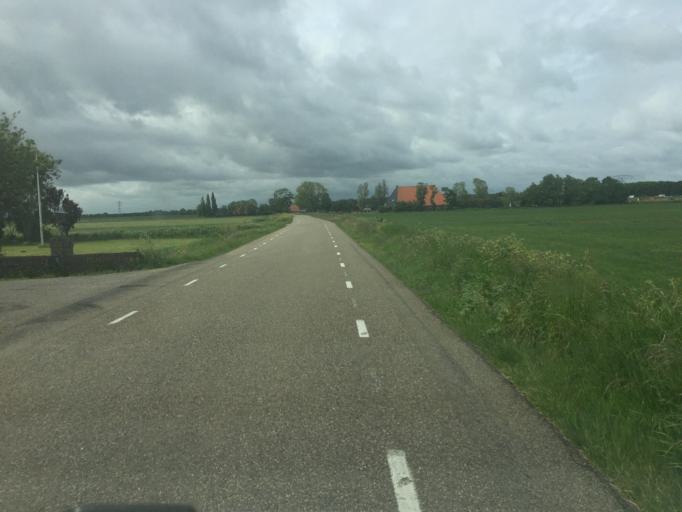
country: NL
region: Friesland
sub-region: Gemeente Lemsterland
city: Lemmer
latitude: 52.8550
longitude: 5.7317
